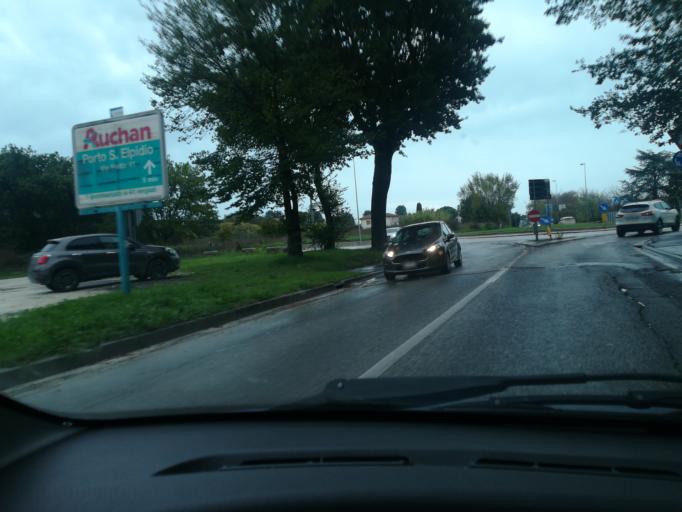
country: IT
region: The Marches
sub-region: Provincia di Macerata
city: Santa Maria Apparente
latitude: 43.2988
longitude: 13.6999
